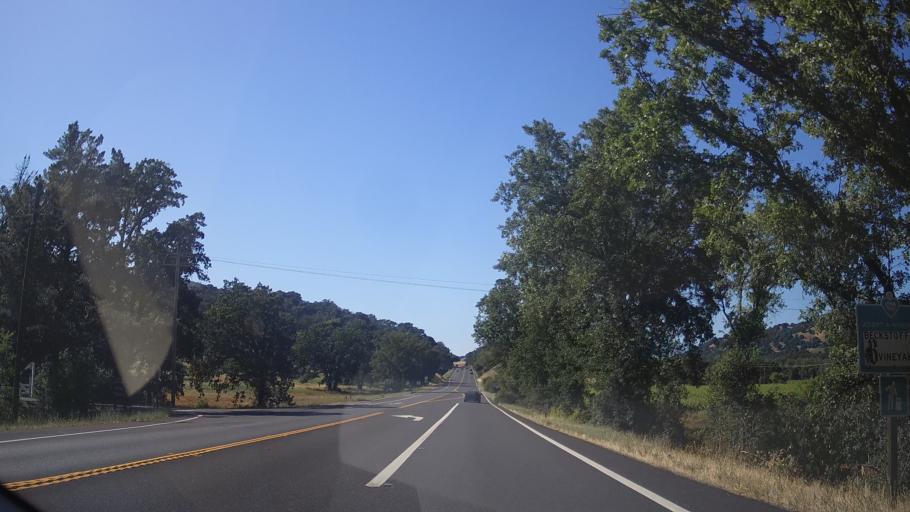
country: US
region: California
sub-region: Mendocino County
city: Talmage
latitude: 39.0032
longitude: -123.1193
